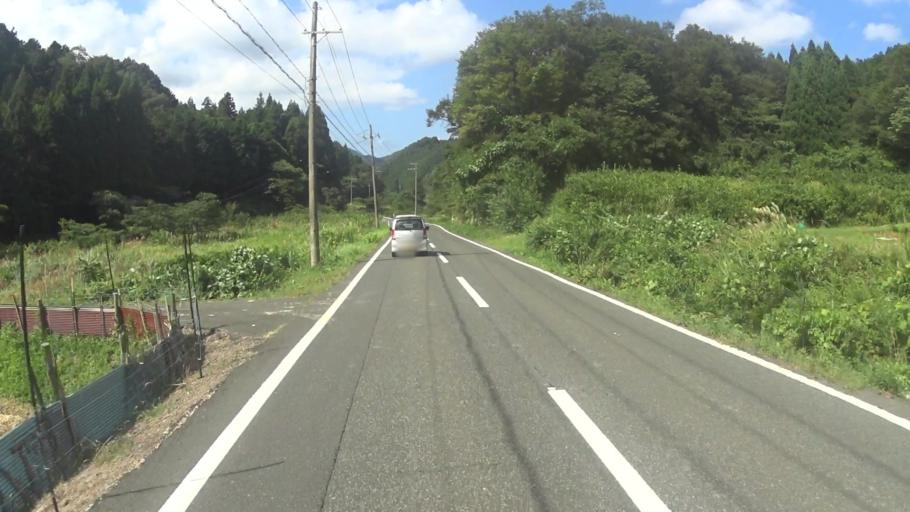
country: JP
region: Kyoto
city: Miyazu
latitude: 35.7131
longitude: 135.2595
